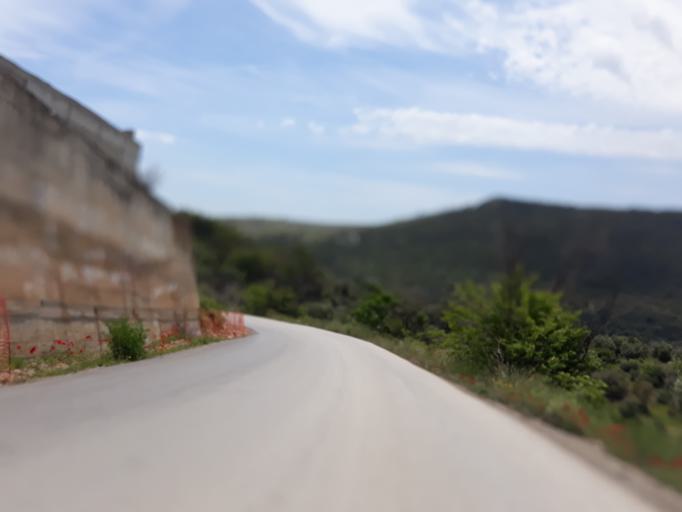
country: GR
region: Attica
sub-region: Nomarchia Dytikis Attikis
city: Magoula
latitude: 38.1480
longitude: 23.5243
